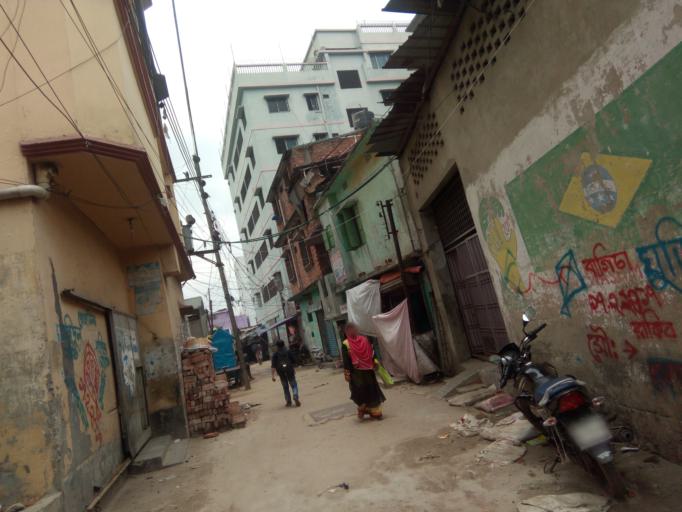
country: BD
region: Dhaka
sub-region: Dhaka
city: Dhaka
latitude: 23.6865
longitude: 90.4383
